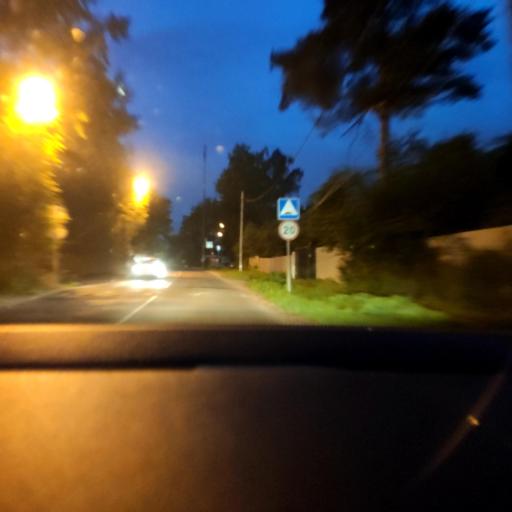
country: RU
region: Moskovskaya
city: Reutov
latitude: 55.7703
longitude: 37.8947
